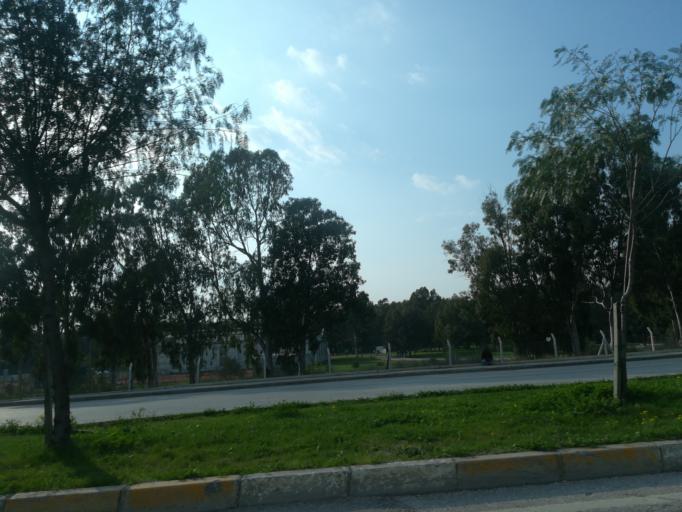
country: TR
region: Adana
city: Adana
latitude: 37.0288
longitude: 35.3451
